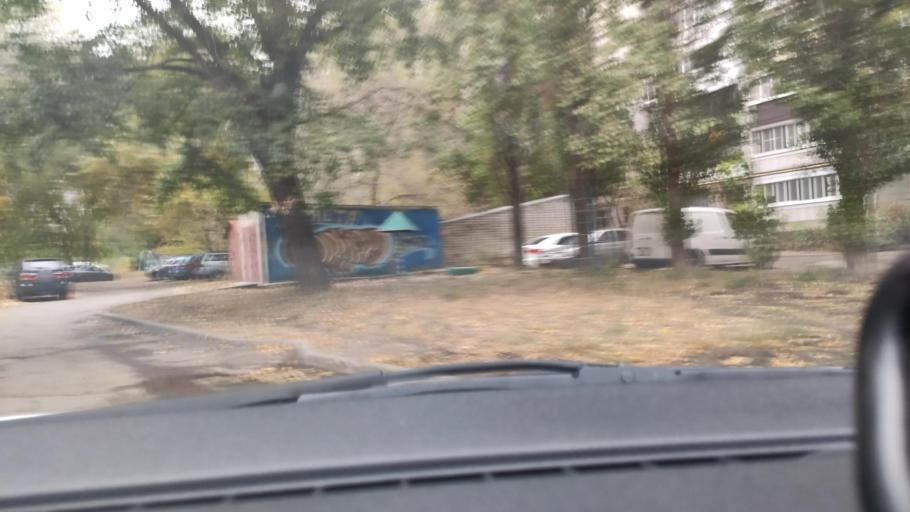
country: RU
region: Voronezj
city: Voronezh
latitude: 51.6848
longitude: 39.1938
